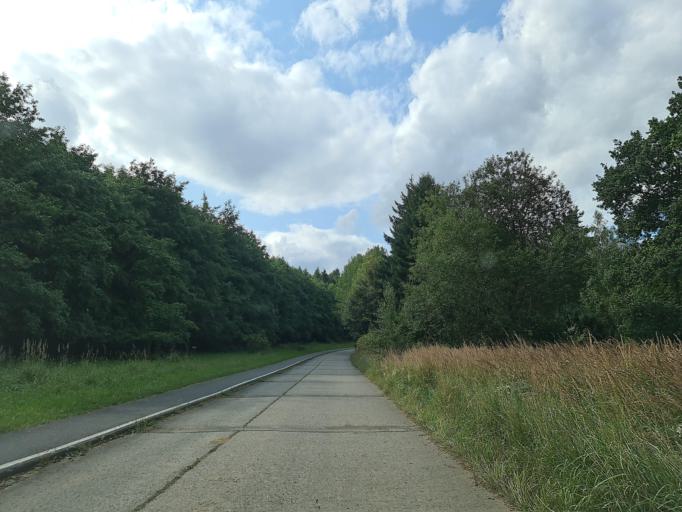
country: DE
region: Saxony
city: Syrau
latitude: 50.5040
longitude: 12.0671
